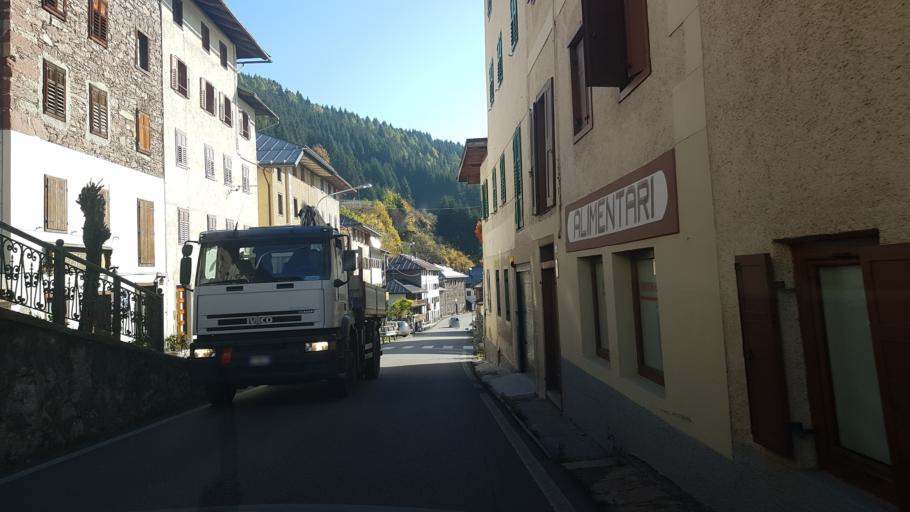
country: IT
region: Veneto
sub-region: Provincia di Belluno
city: Candide
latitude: 46.5995
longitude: 12.4927
